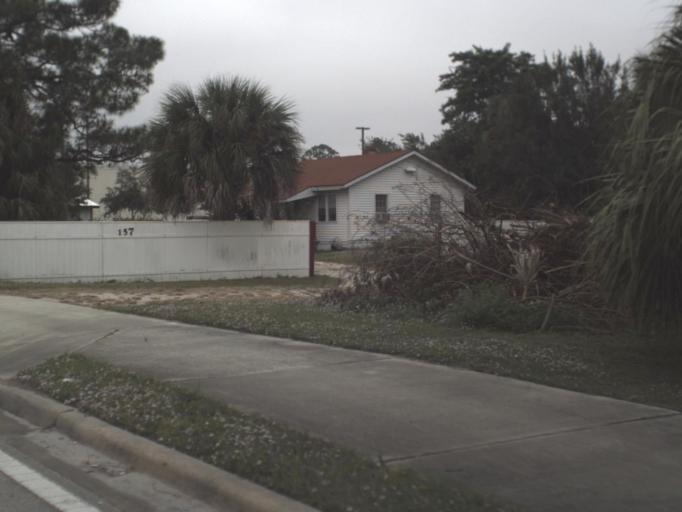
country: US
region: Florida
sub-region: Brevard County
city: June Park
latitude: 27.9992
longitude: -80.6732
